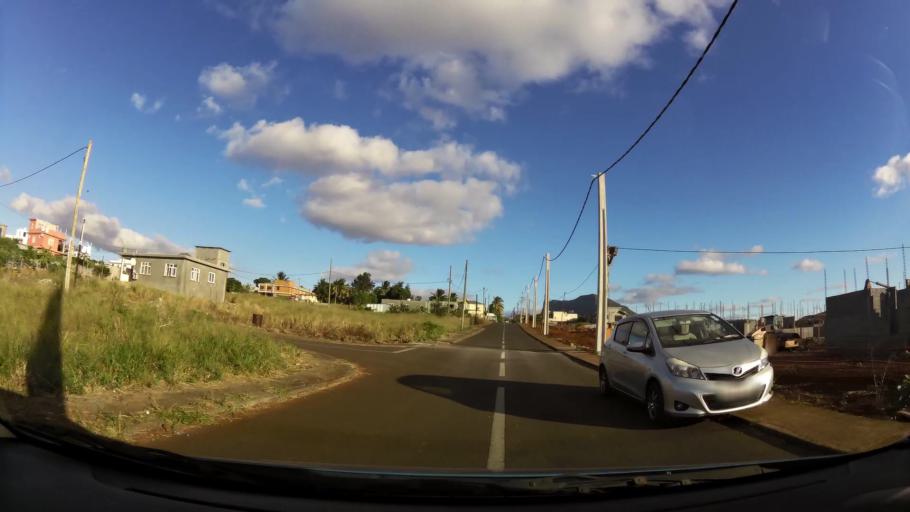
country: MU
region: Black River
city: Petite Riviere
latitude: -20.2148
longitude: 57.4621
